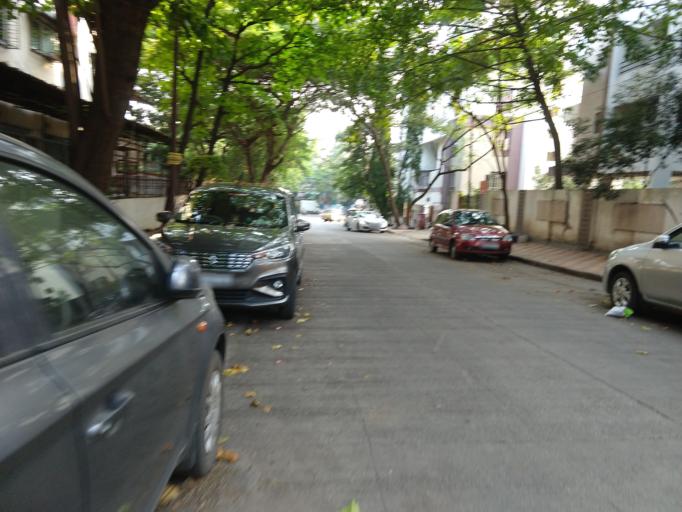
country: IN
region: Maharashtra
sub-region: Pune Division
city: Shivaji Nagar
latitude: 18.5098
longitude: 73.7932
